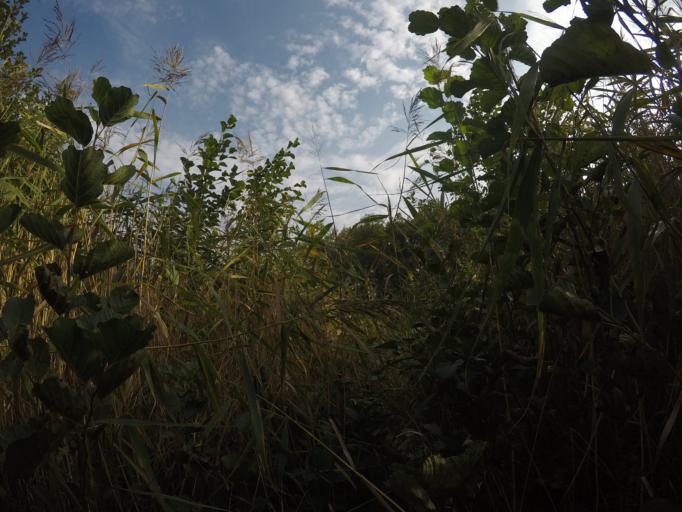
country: SE
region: Soedermanland
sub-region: Eskilstuna Kommun
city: Kvicksund
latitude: 59.4676
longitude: 16.2243
